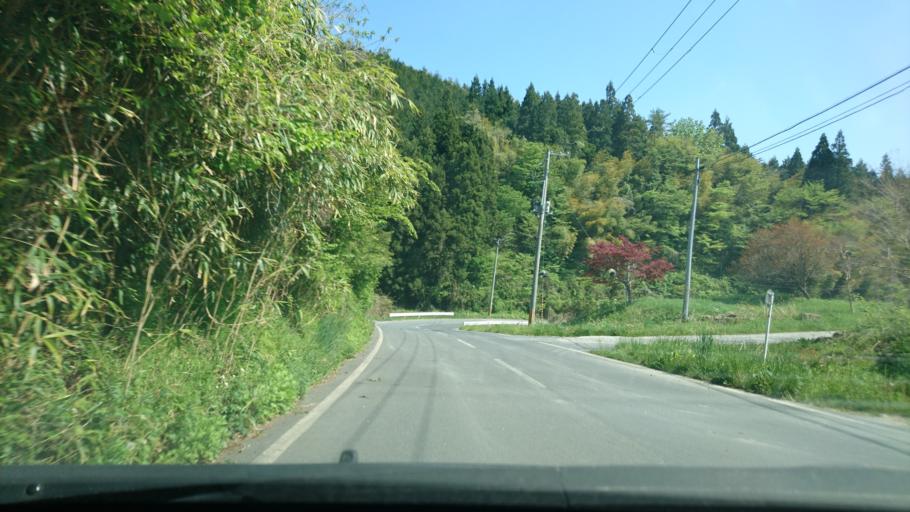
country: JP
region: Iwate
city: Ichinoseki
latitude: 38.9353
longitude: 141.2793
